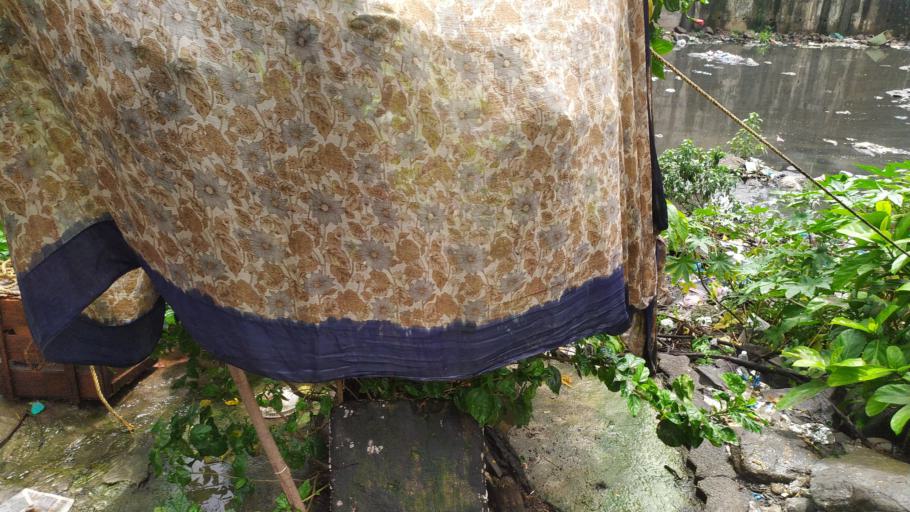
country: IN
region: Maharashtra
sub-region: Mumbai Suburban
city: Borivli
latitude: 19.2386
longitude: 72.8564
